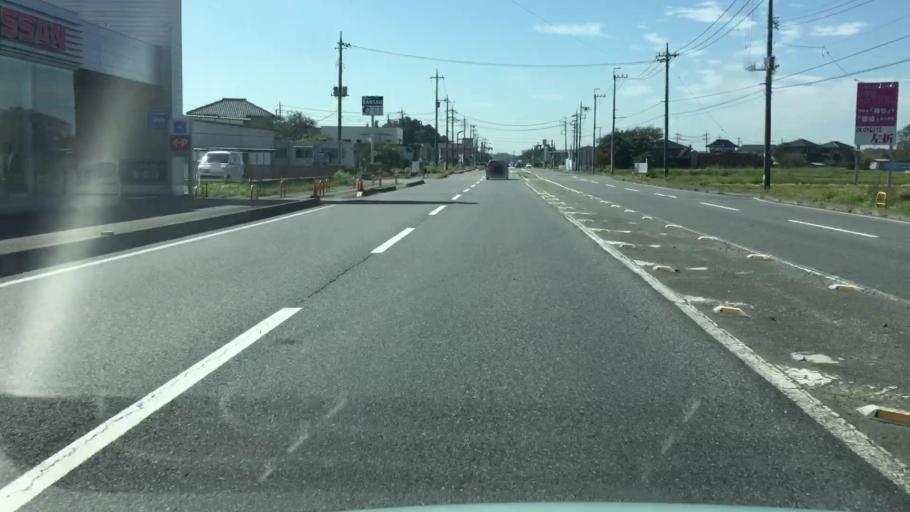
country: JP
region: Ibaraki
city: Ryugasaki
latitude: 35.9037
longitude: 140.1696
